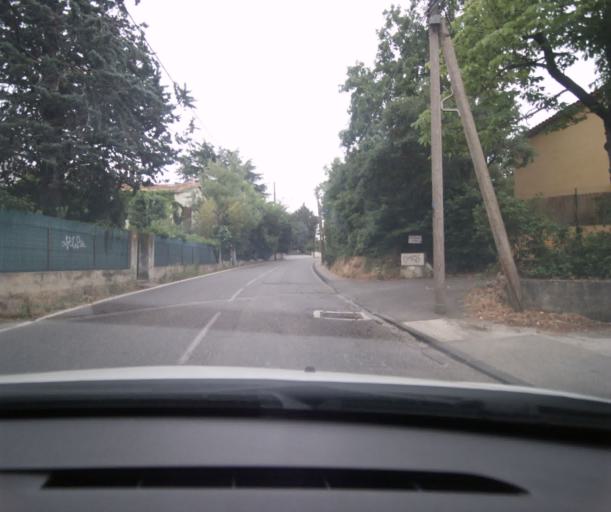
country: FR
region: Provence-Alpes-Cote d'Azur
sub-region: Departement du Var
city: La Valette-du-Var
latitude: 43.1119
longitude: 5.9802
